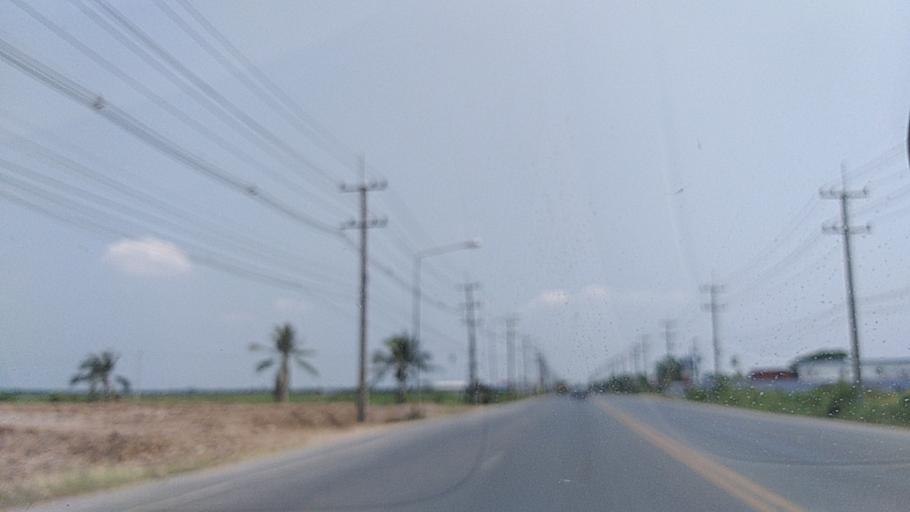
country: TH
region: Bangkok
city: Nong Chok
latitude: 13.9670
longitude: 100.9383
